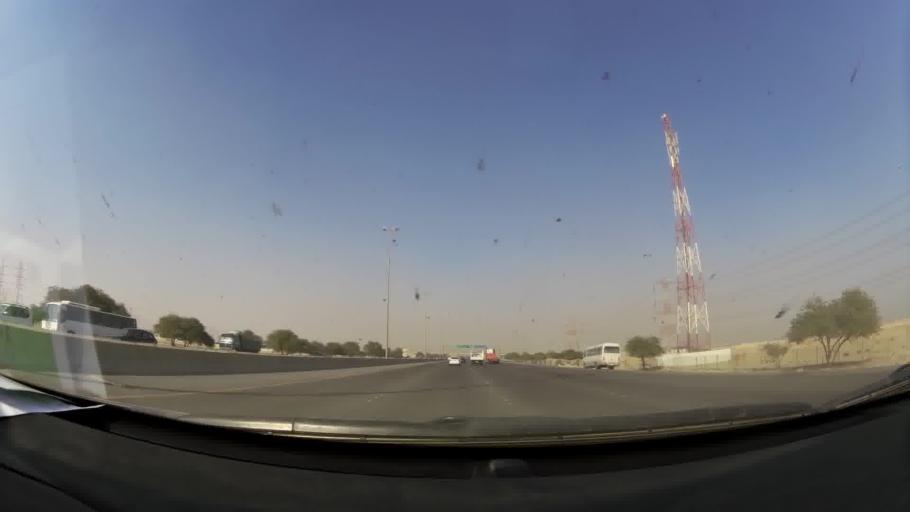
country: KW
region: Al Ahmadi
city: Al Ahmadi
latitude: 29.0206
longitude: 48.0922
